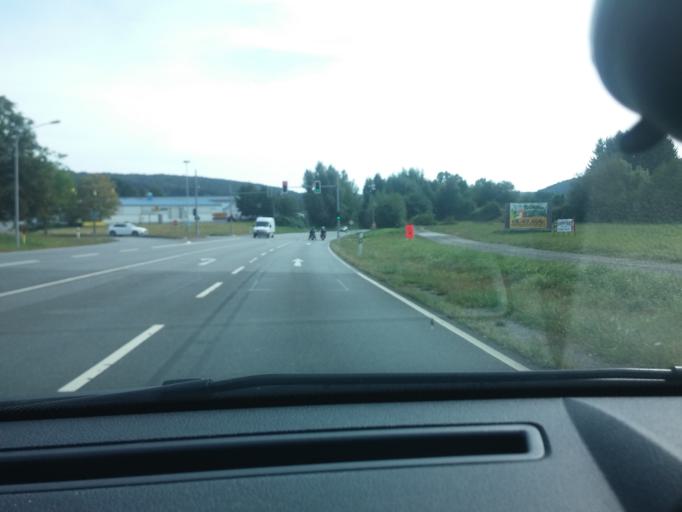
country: DE
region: Hesse
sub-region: Regierungsbezirk Darmstadt
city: Bad Konig
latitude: 49.7492
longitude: 9.0019
